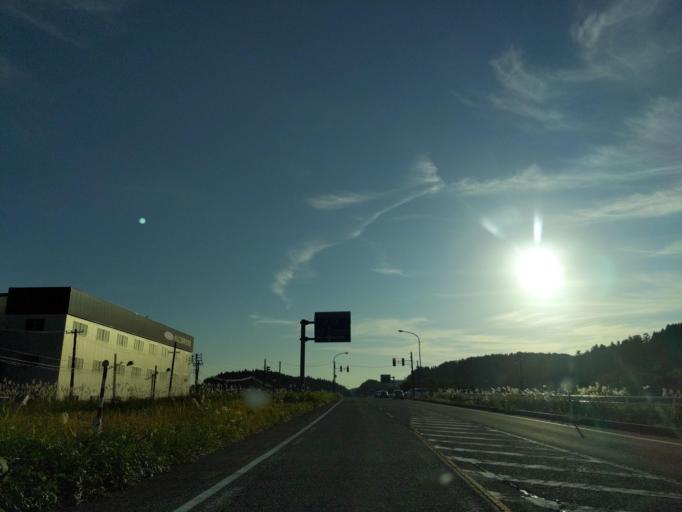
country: JP
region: Niigata
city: Nagaoka
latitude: 37.5718
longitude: 138.7440
